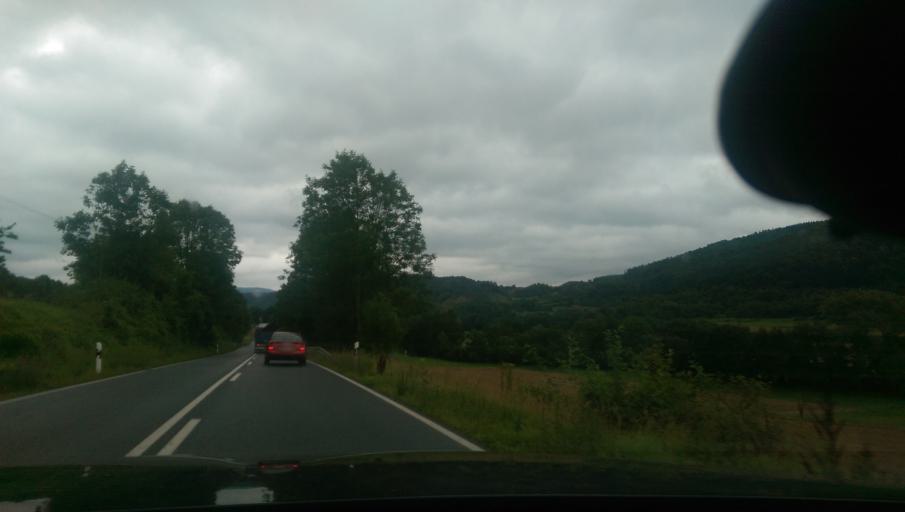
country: DE
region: Hesse
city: Witzenhausen
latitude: 51.2810
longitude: 9.8431
